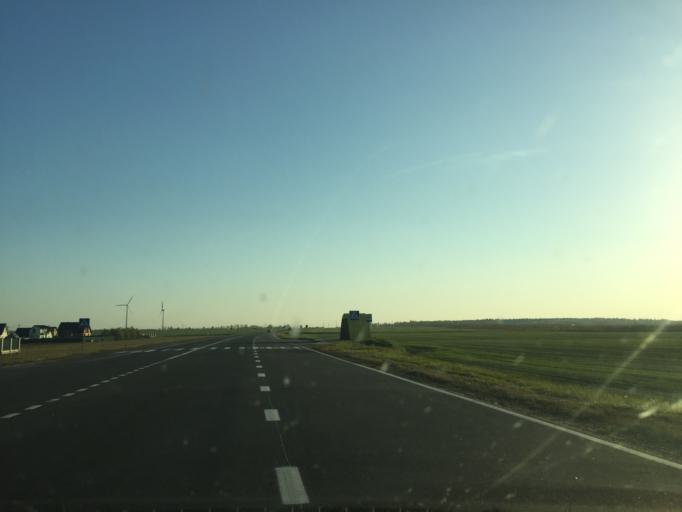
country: BY
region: Mogilev
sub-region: Mahilyowski Rayon
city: Kadino
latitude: 53.8788
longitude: 30.4879
